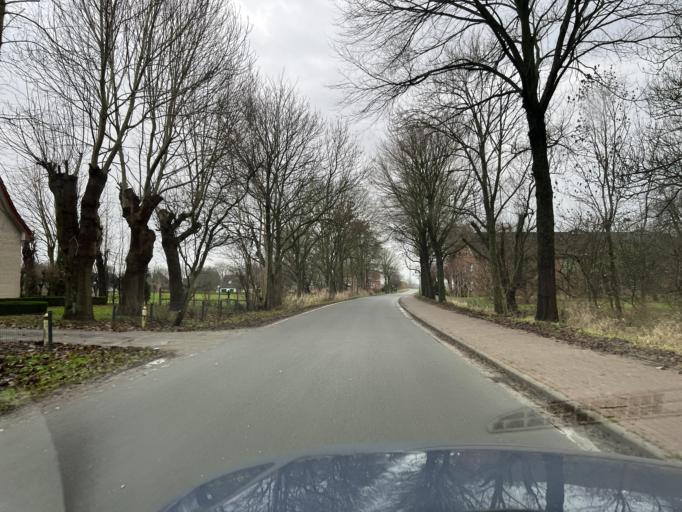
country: DE
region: Schleswig-Holstein
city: Norddeich
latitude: 54.2143
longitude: 8.8956
